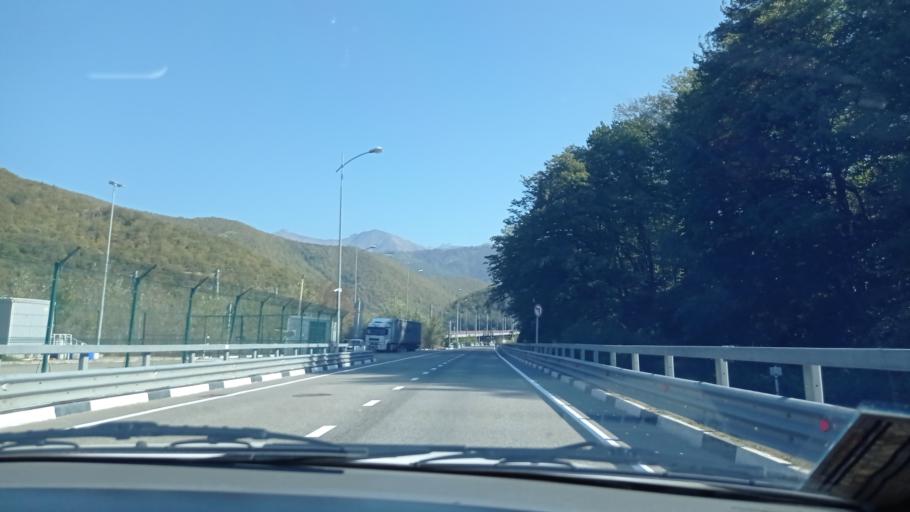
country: RU
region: Krasnodarskiy
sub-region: Sochi City
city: Krasnaya Polyana
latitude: 43.6833
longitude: 40.2351
